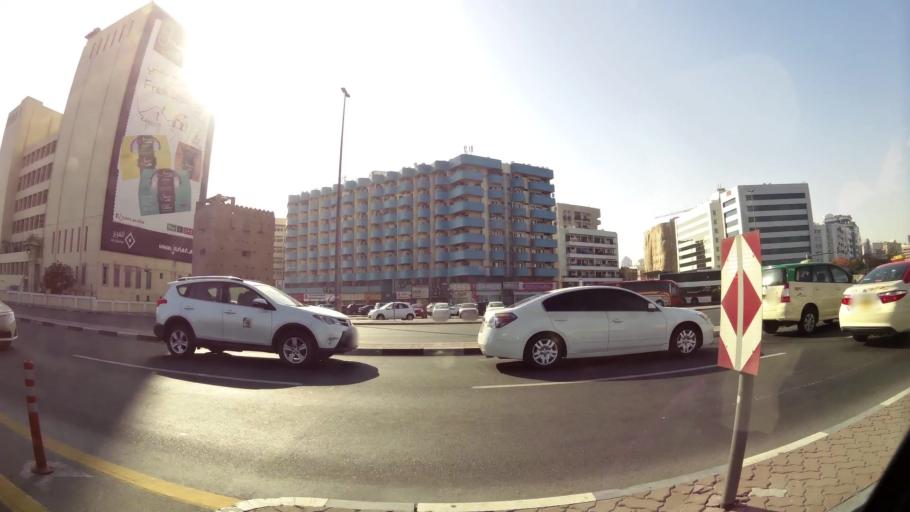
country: AE
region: Ash Shariqah
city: Sharjah
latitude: 25.2615
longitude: 55.2842
